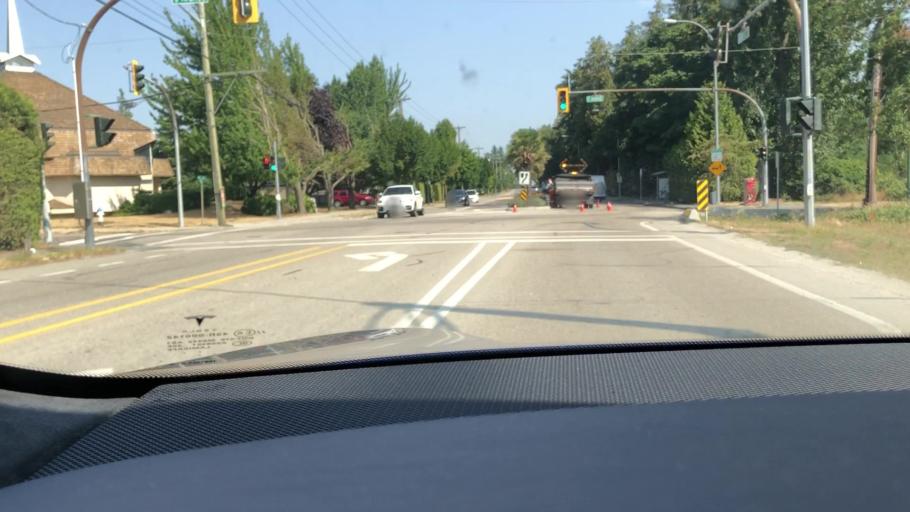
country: US
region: Washington
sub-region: Whatcom County
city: Point Roberts
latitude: 49.0135
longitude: -123.0686
